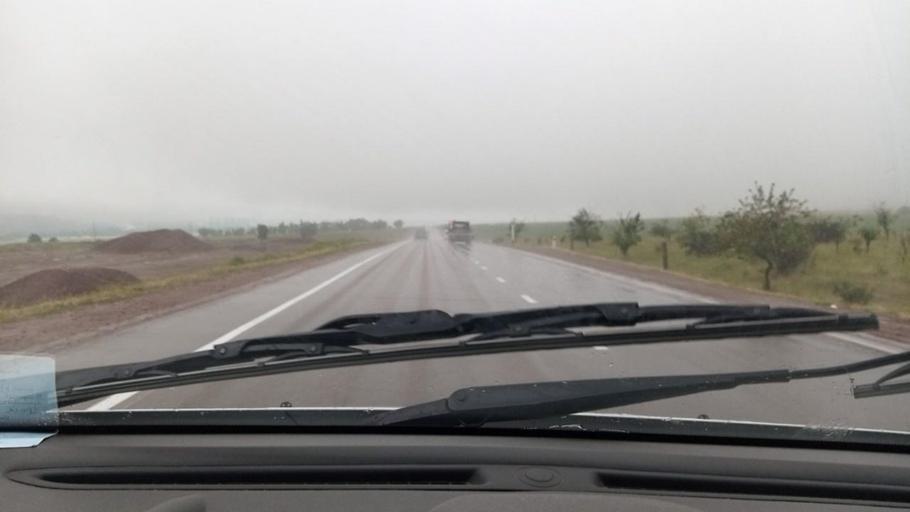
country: UZ
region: Toshkent
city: Angren
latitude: 41.0459
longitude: 70.1534
